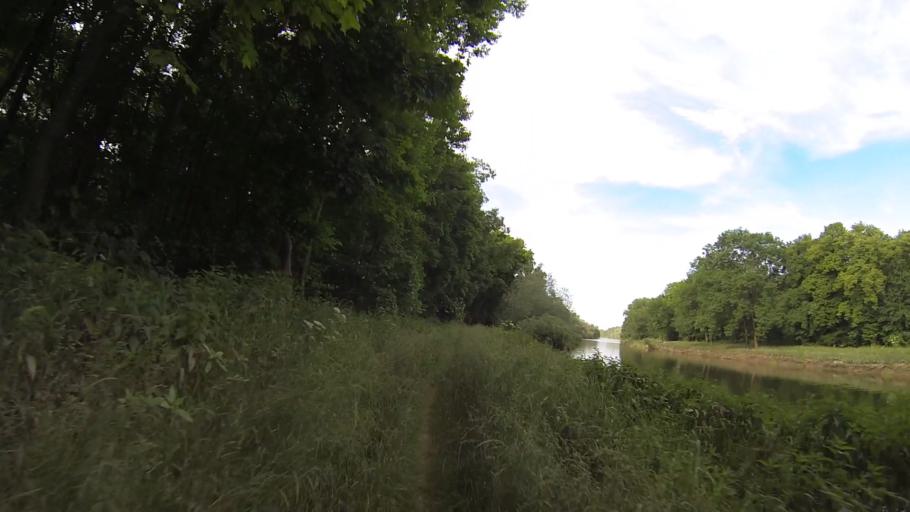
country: DE
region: Baden-Wuerttemberg
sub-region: Tuebingen Region
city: Ulm
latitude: 48.3785
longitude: 9.9654
